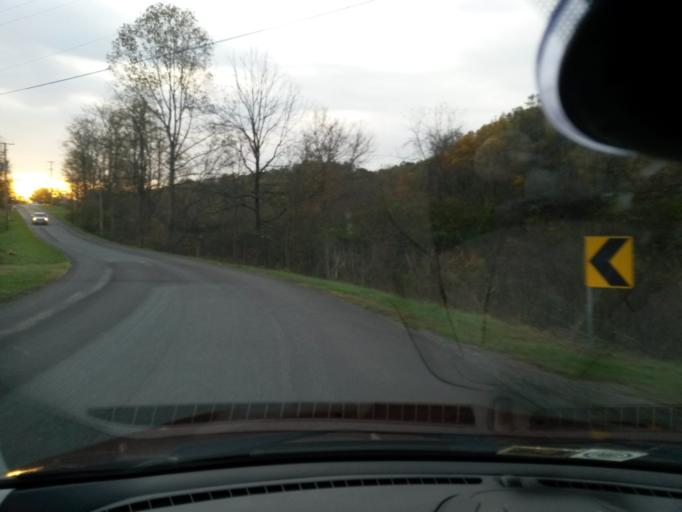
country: US
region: Virginia
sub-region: Roanoke County
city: Narrows
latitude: 37.1671
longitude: -79.8709
